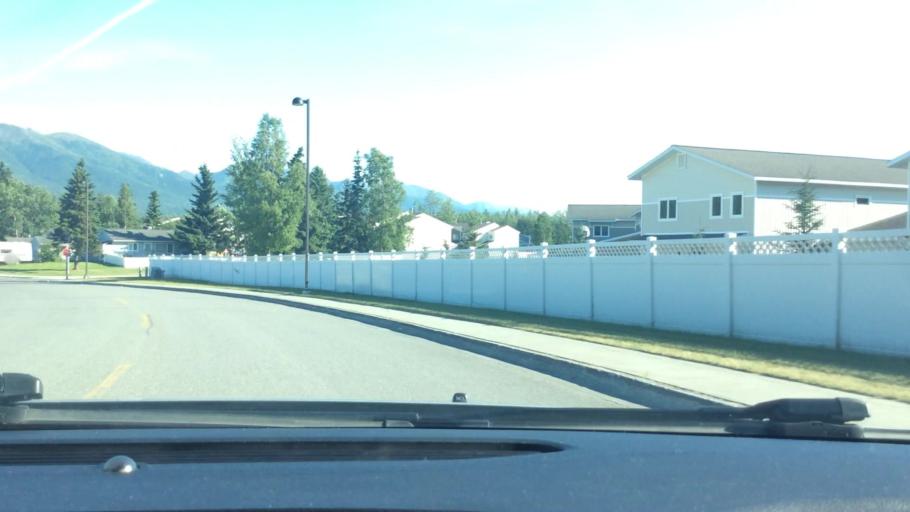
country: US
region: Alaska
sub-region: Anchorage Municipality
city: Elmendorf Air Force Base
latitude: 61.2488
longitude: -149.7021
